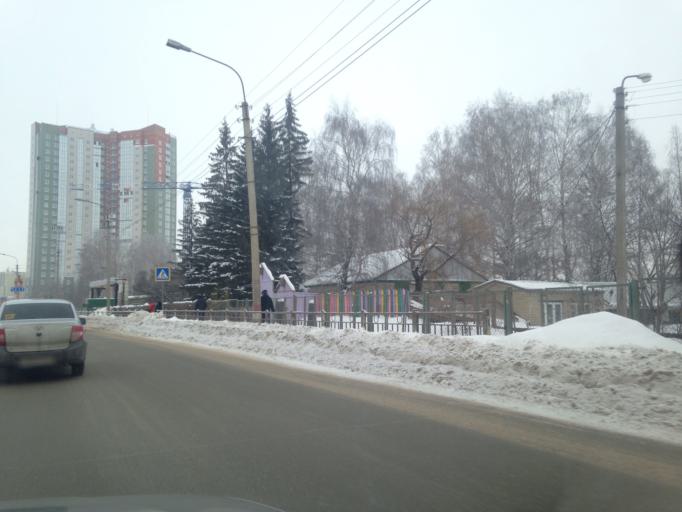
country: RU
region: Ulyanovsk
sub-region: Ulyanovskiy Rayon
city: Ulyanovsk
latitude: 54.3022
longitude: 48.3478
